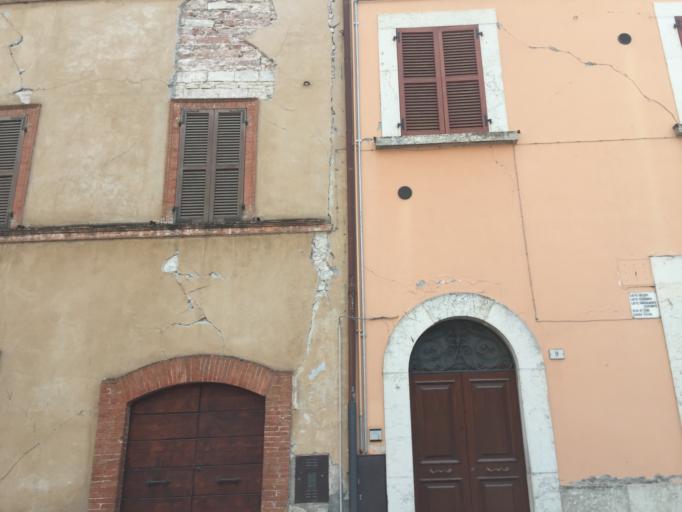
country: IT
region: The Marches
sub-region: Provincia di Macerata
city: Visso
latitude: 42.9310
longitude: 13.0865
